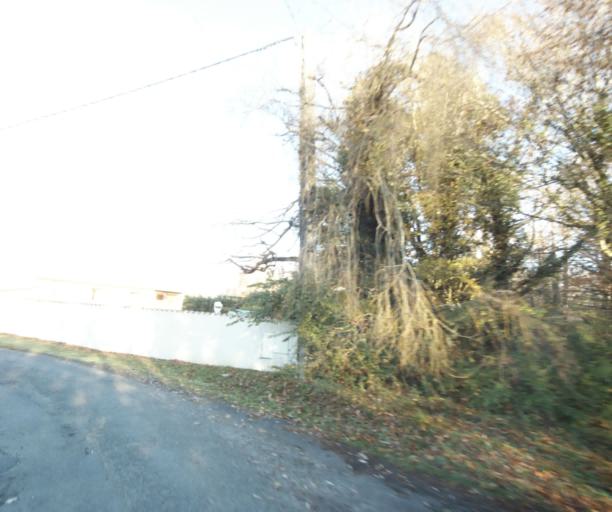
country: FR
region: Poitou-Charentes
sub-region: Departement de la Charente-Maritime
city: Cherac
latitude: 45.7273
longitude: -0.4717
